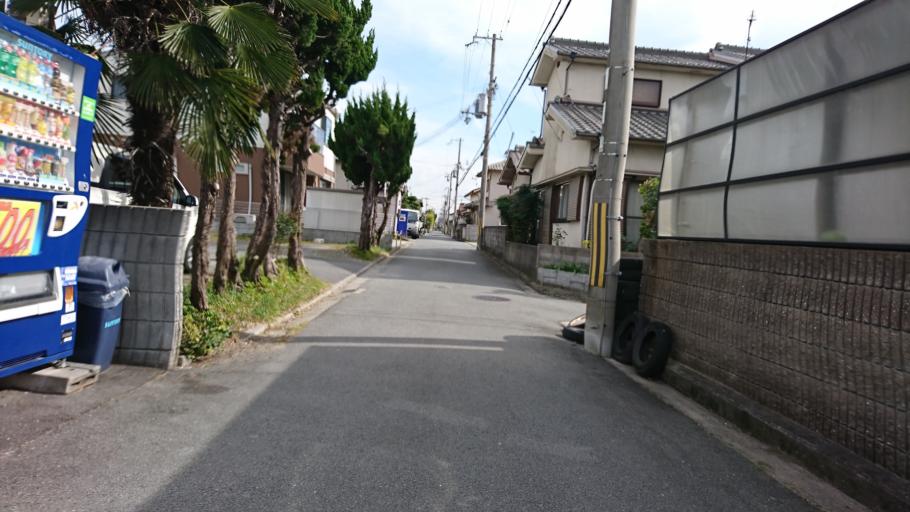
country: JP
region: Hyogo
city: Kakogawacho-honmachi
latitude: 34.7441
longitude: 134.8134
